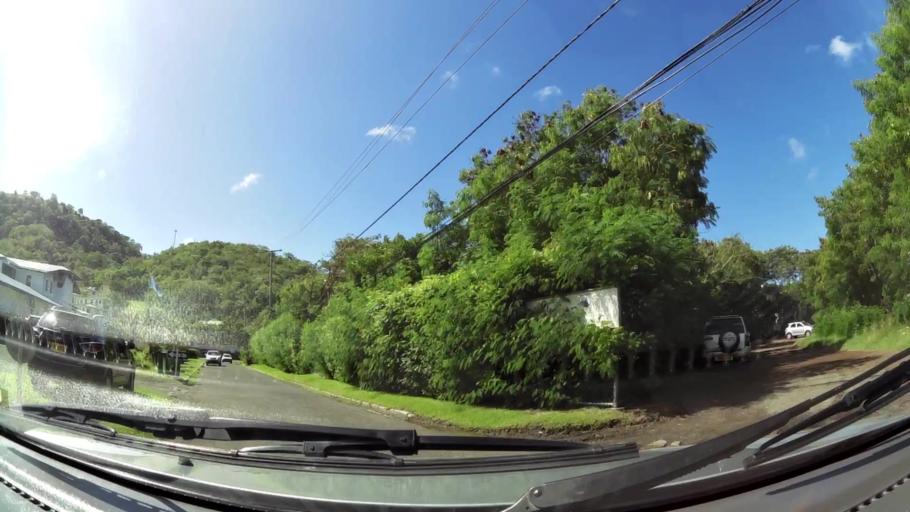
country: GD
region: Saint George
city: Saint George's
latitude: 12.0215
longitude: -61.7657
